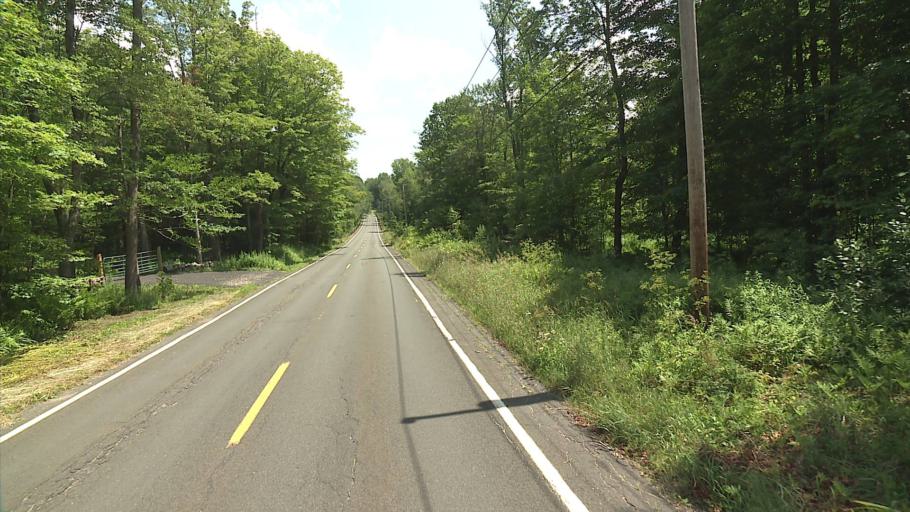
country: US
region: Connecticut
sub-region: Litchfield County
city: Winchester Center
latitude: 41.9887
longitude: -73.1446
